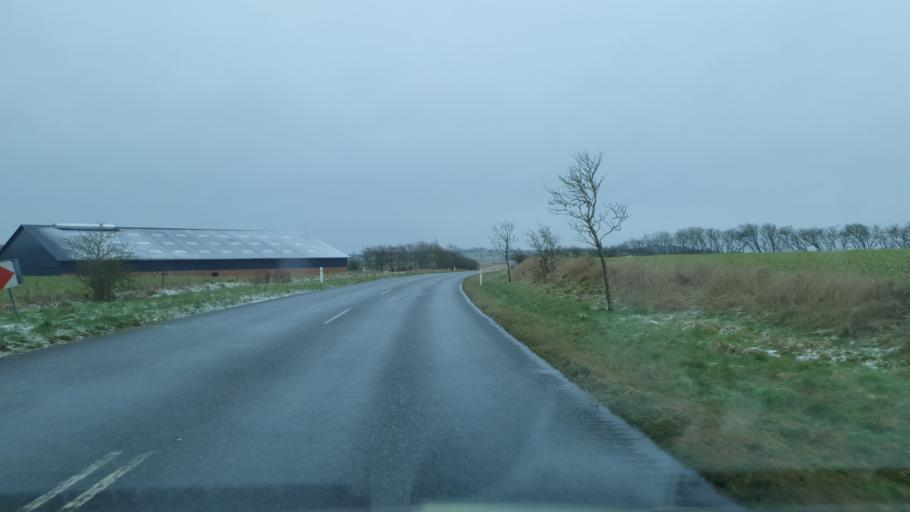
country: DK
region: North Denmark
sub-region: Jammerbugt Kommune
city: Brovst
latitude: 57.1245
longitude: 9.4888
